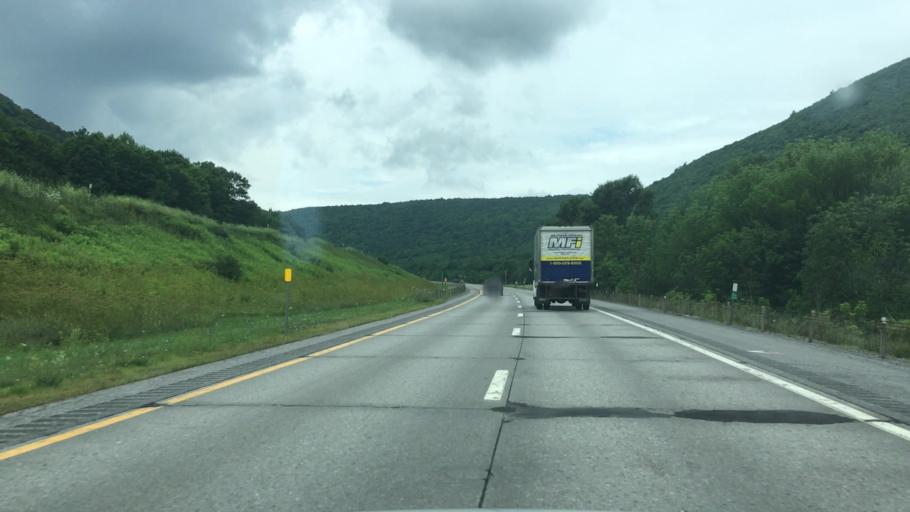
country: US
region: New York
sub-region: Otsego County
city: Worcester
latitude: 42.6502
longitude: -74.6303
